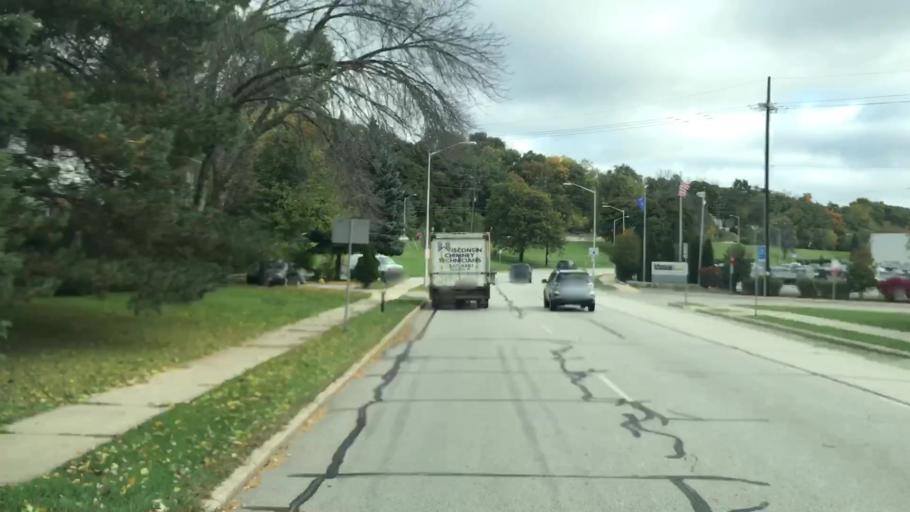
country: US
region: Wisconsin
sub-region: Waukesha County
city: Waukesha
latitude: 43.0174
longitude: -88.2295
